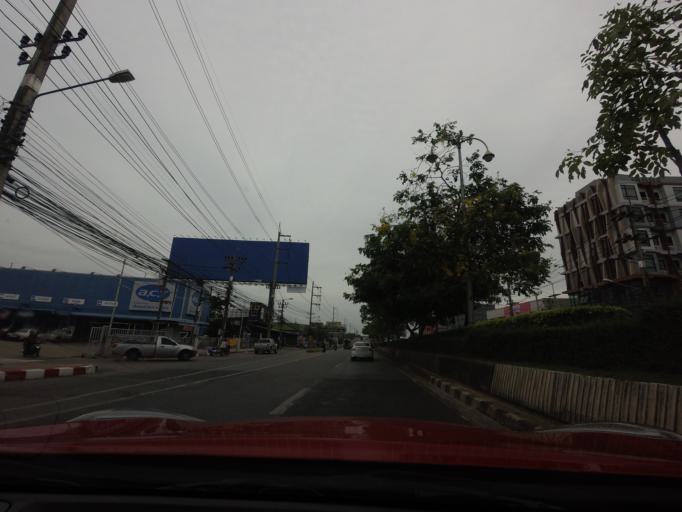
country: TH
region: Songkhla
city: Hat Yai
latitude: 6.9904
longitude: 100.4827
